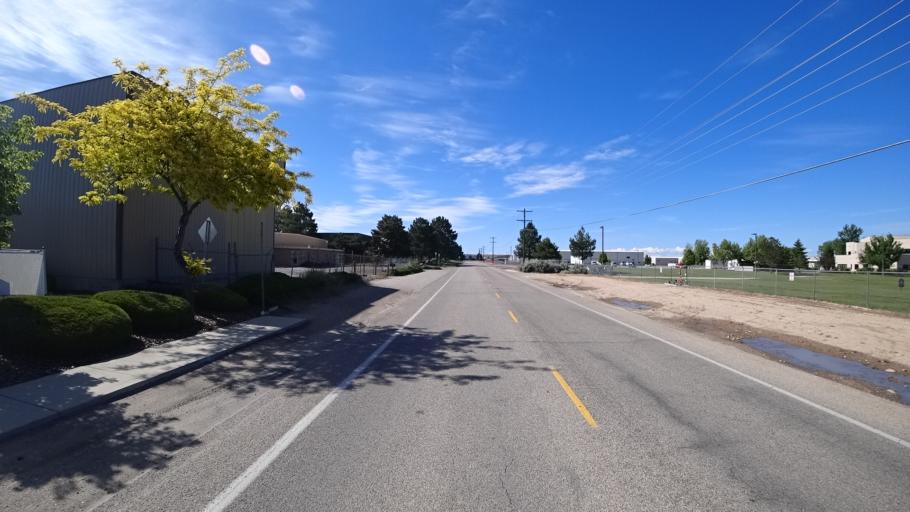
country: US
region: Idaho
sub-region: Ada County
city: Boise
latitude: 43.5678
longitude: -116.2074
